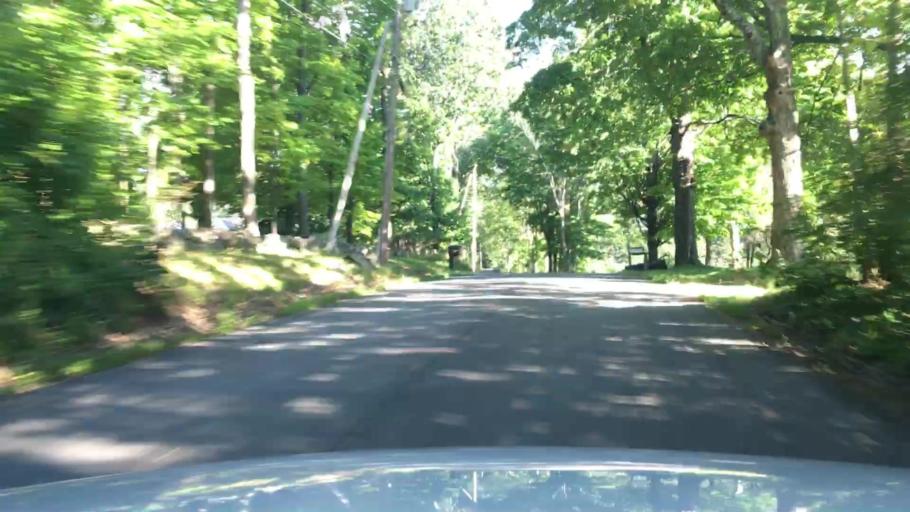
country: US
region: New Hampshire
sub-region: Strafford County
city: Madbury
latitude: 43.1600
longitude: -70.9286
